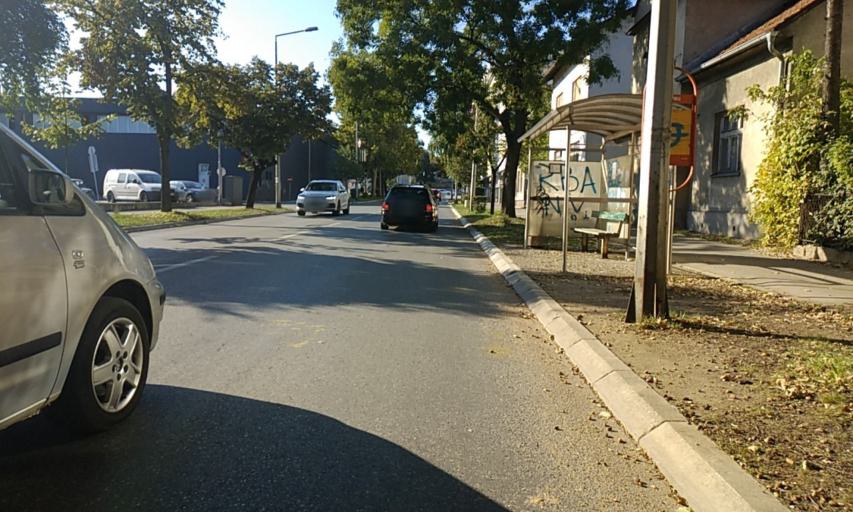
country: BA
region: Republika Srpska
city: Banja Luka
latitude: 44.7772
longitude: 17.1868
